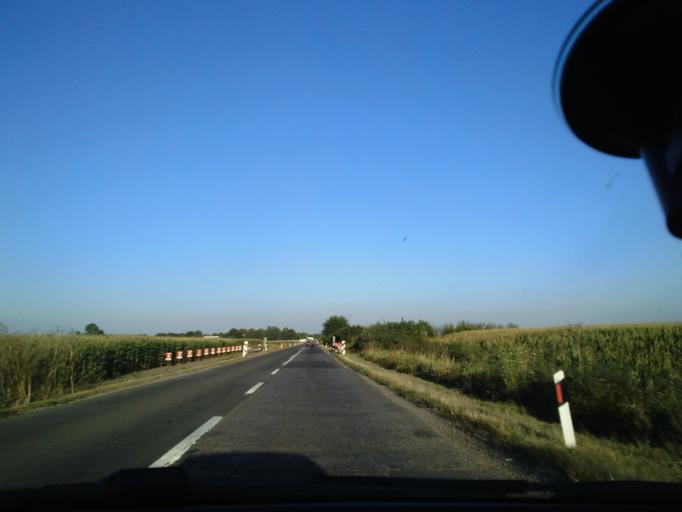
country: RS
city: Kisac
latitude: 45.3382
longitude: 19.6611
